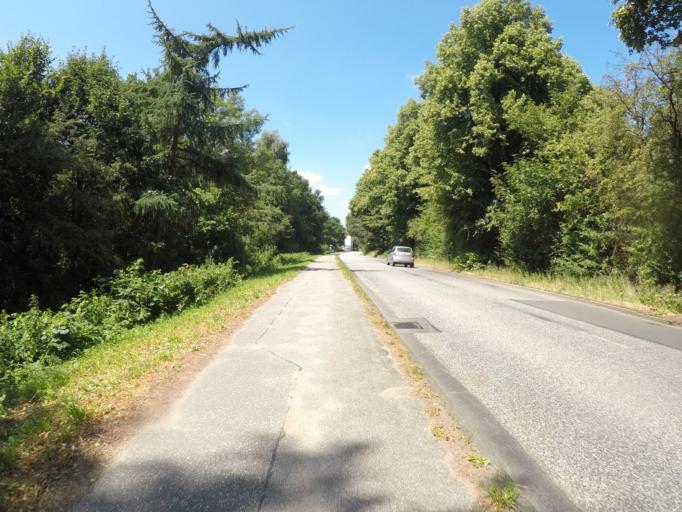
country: DE
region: Hamburg
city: Rothenburgsort
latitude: 53.5051
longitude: 10.0248
